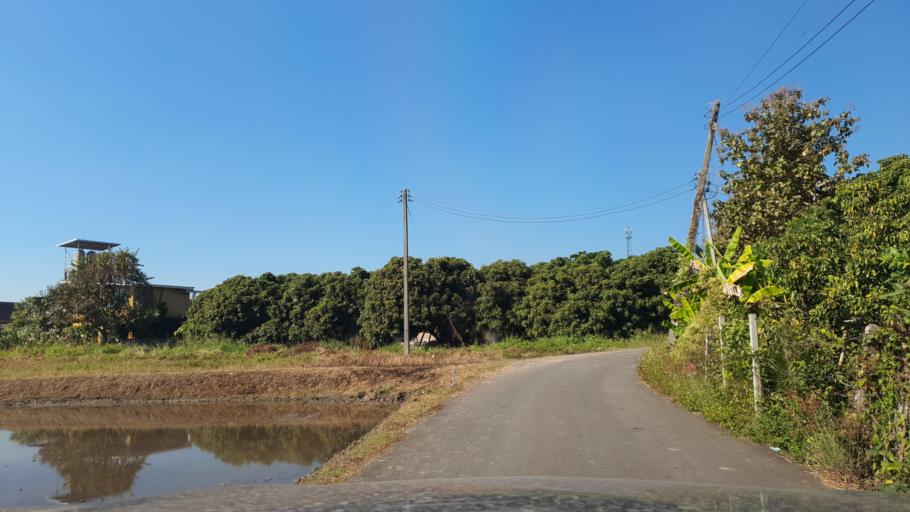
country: TH
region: Chiang Mai
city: San Pa Tong
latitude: 18.6504
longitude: 98.8675
